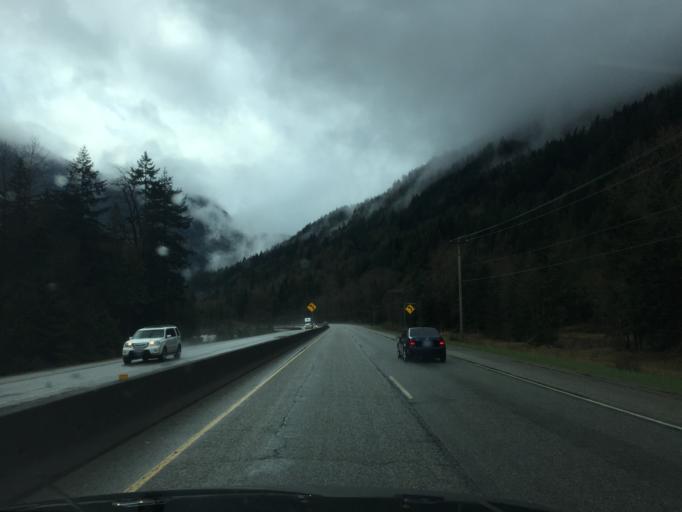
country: CA
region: British Columbia
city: Hope
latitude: 49.3984
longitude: -121.3175
